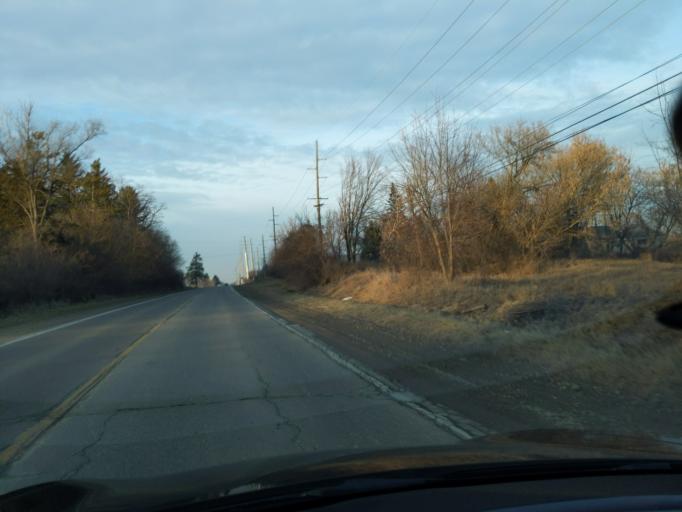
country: US
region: Michigan
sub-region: Livingston County
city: Brighton
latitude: 42.6242
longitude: -83.7522
